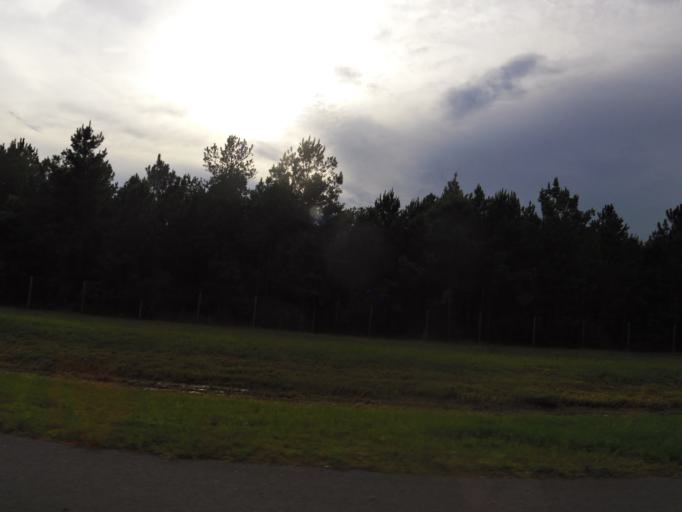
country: US
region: Florida
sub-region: Clay County
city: Middleburg
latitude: 30.1058
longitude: -81.8357
